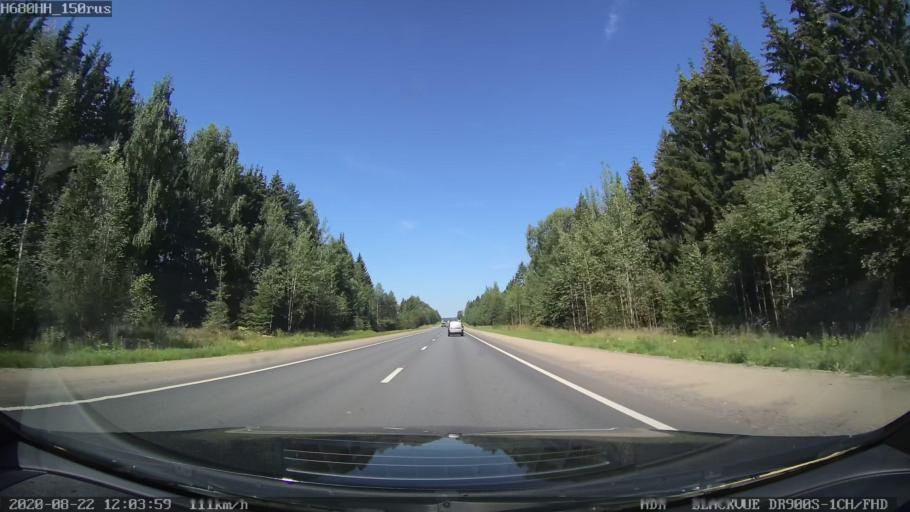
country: RU
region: Tverskaya
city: Rameshki
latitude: 57.2624
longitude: 36.0783
